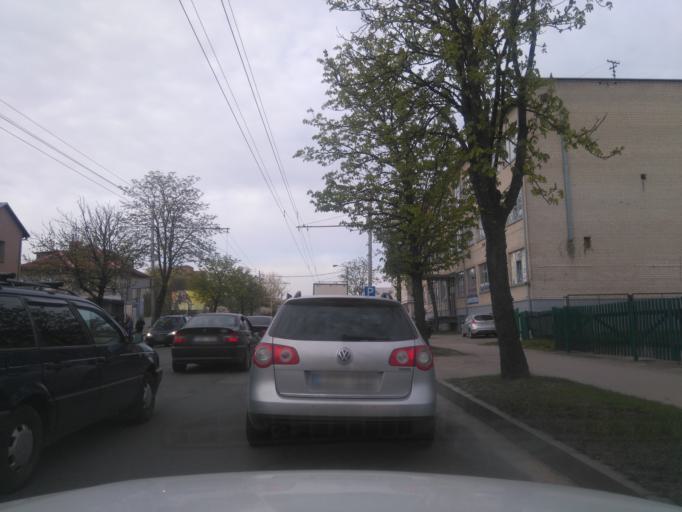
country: LT
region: Kauno apskritis
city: Dainava (Kaunas)
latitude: 54.9043
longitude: 23.9739
